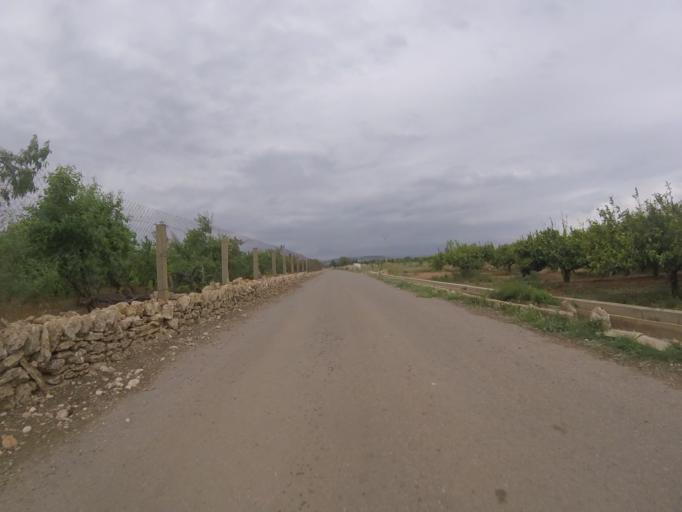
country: ES
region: Valencia
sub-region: Provincia de Castello
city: Torreblanca
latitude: 40.2162
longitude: 0.2317
